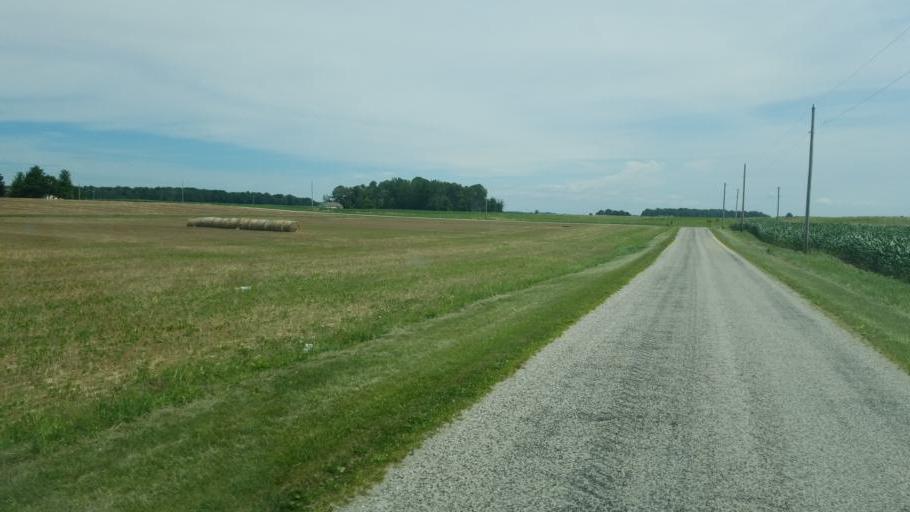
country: US
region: Ohio
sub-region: Crawford County
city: Bucyrus
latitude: 40.8742
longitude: -82.9233
